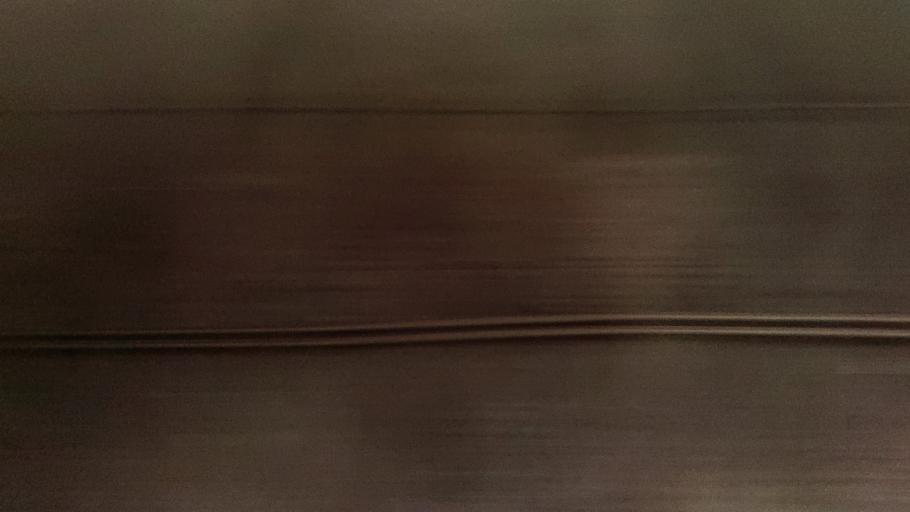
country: TW
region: Taiwan
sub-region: Keelung
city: Keelung
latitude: 25.0875
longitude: 121.7060
